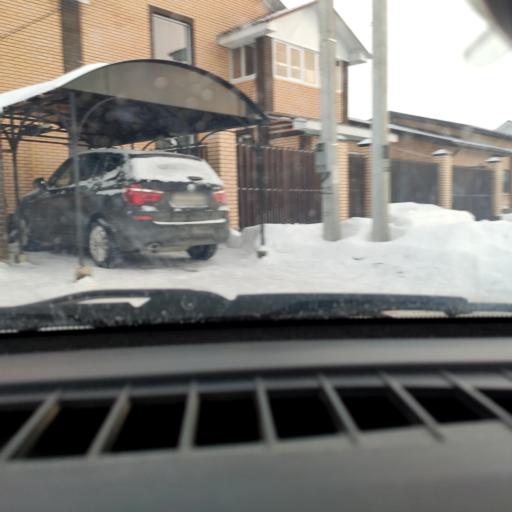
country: RU
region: Bashkortostan
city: Kabakovo
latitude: 54.6122
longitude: 56.1203
